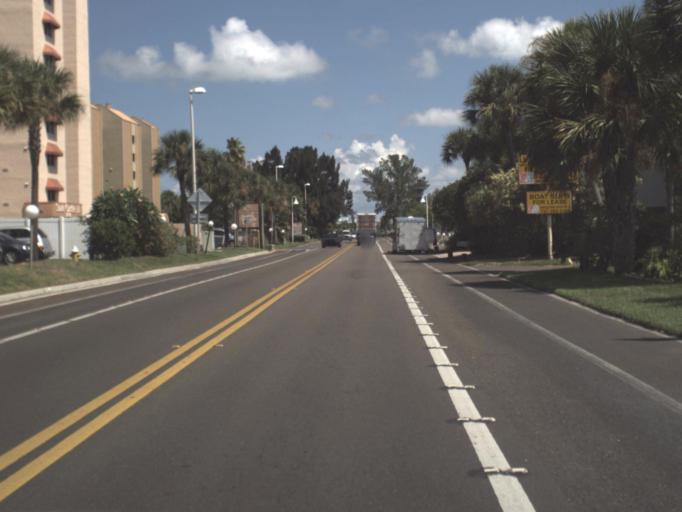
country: US
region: Florida
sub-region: Pinellas County
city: Indian Shores
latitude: 27.8662
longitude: -82.8488
